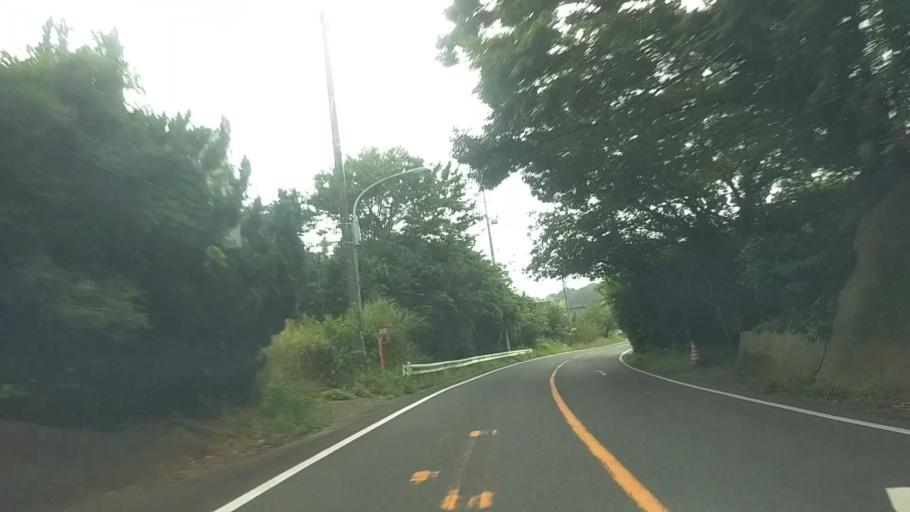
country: JP
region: Chiba
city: Kimitsu
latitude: 35.2207
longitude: 139.9097
